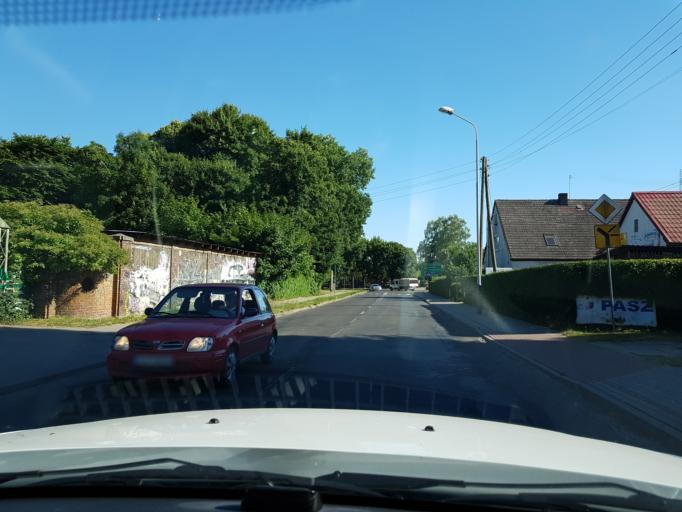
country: PL
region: West Pomeranian Voivodeship
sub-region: Powiat lobeski
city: Lobez
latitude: 53.6440
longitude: 15.6170
